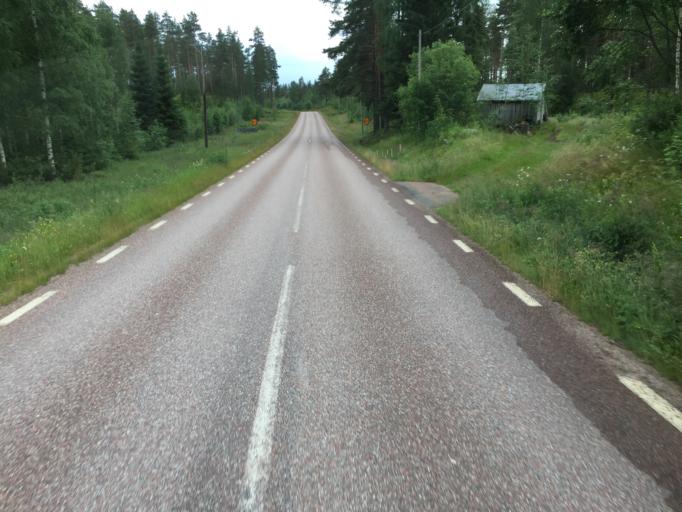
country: SE
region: Dalarna
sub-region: Vansbro Kommun
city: Vansbro
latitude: 60.7627
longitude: 14.1437
